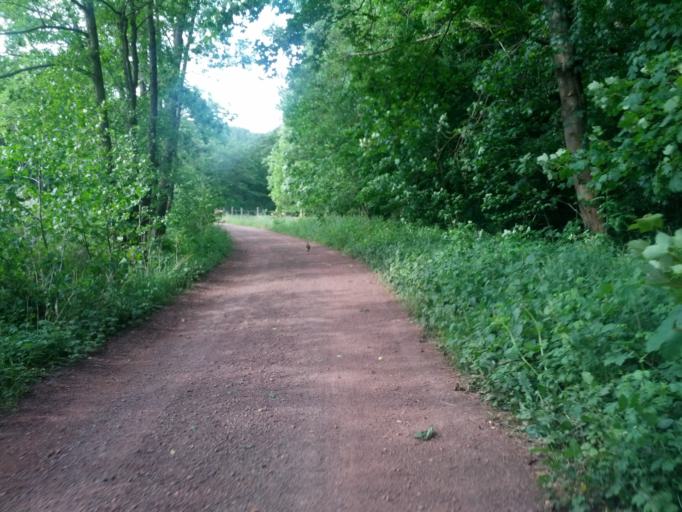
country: DE
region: Thuringia
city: Eisenach
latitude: 50.9416
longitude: 10.3445
